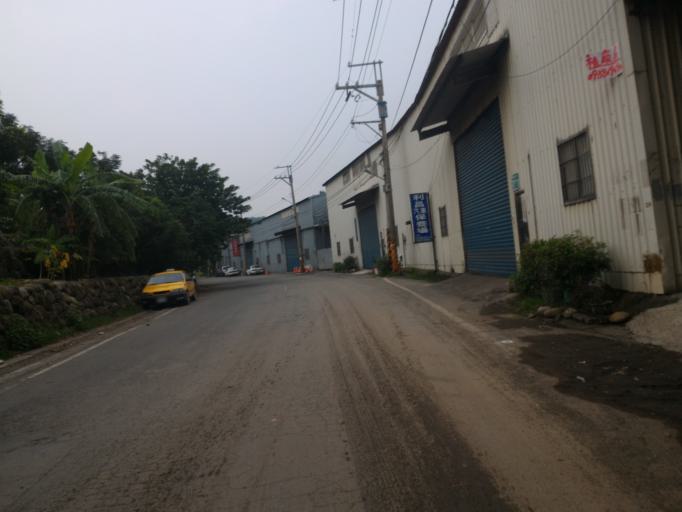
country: TW
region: Taipei
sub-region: Taipei
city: Banqiao
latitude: 24.9600
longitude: 121.4092
